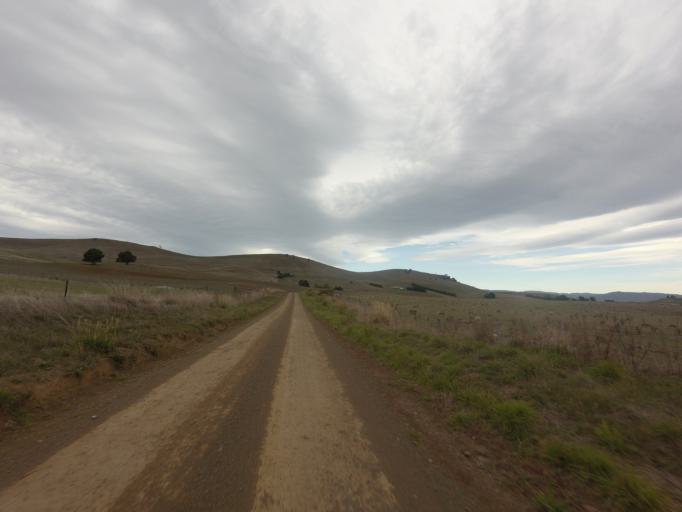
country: AU
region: Tasmania
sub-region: Derwent Valley
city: New Norfolk
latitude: -42.4453
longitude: 146.7979
